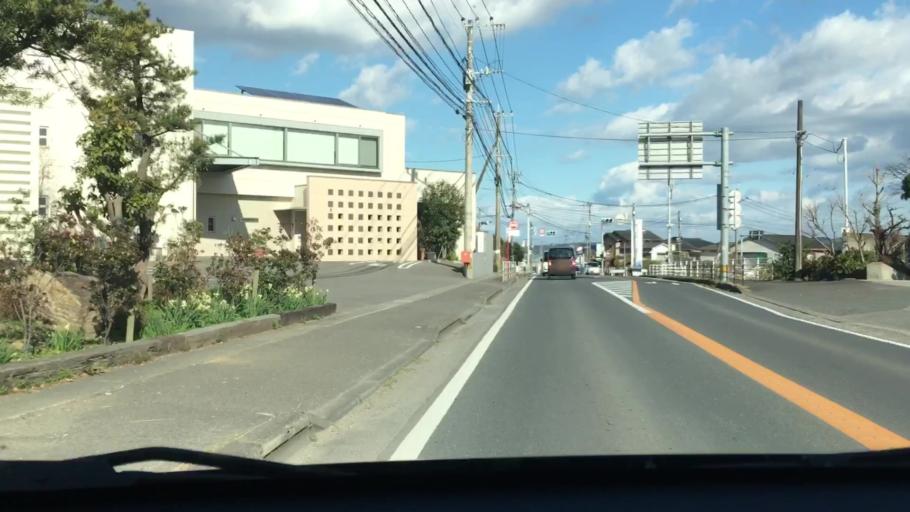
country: JP
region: Oita
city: Tsurusaki
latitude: 33.1767
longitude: 131.6616
